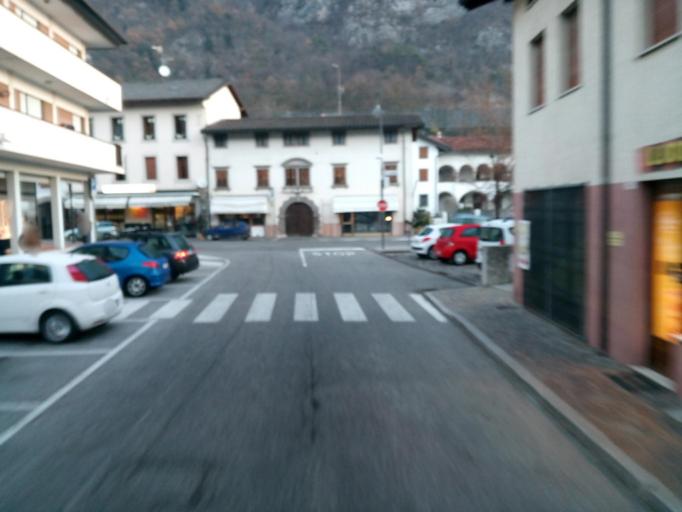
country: IT
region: Friuli Venezia Giulia
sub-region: Provincia di Udine
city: Villa Santina
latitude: 46.4156
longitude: 12.9243
